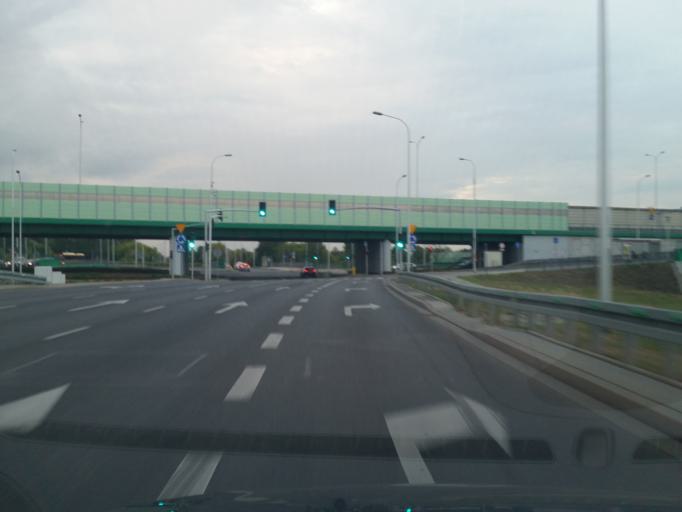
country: PL
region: Masovian Voivodeship
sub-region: Warszawa
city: Bielany
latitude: 52.3003
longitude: 20.9405
